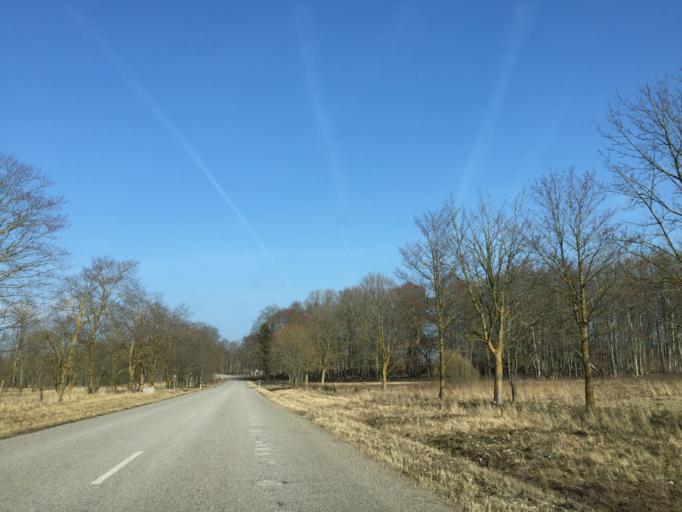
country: EE
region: Saare
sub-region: Kuressaare linn
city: Kuressaare
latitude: 58.0163
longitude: 22.0744
